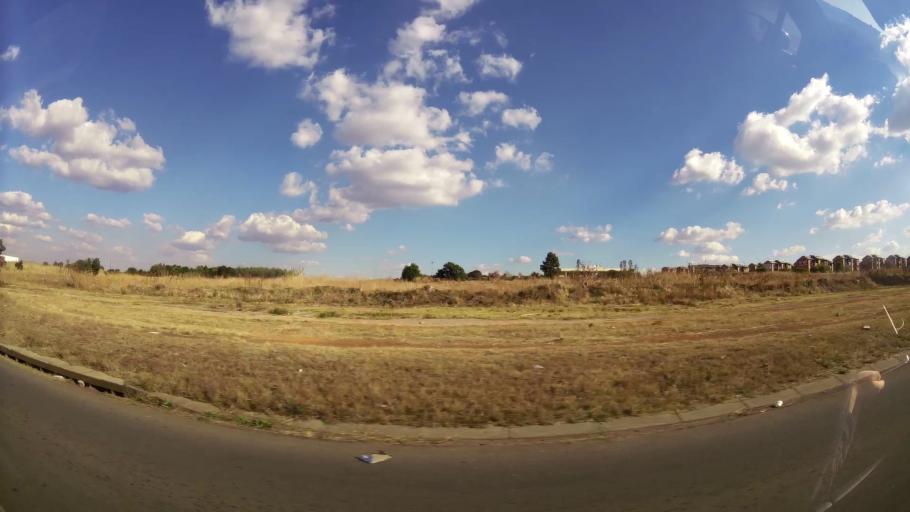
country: ZA
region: Mpumalanga
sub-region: Nkangala District Municipality
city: Witbank
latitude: -25.8824
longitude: 29.2580
